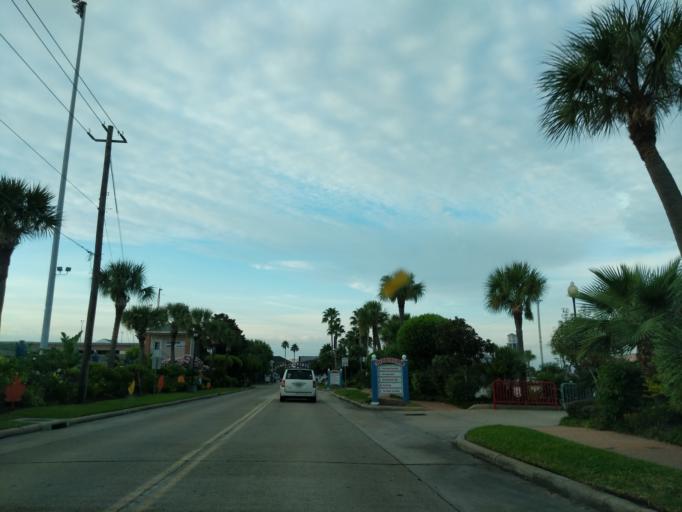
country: US
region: Texas
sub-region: Galveston County
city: Kemah
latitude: 29.5458
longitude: -95.0188
